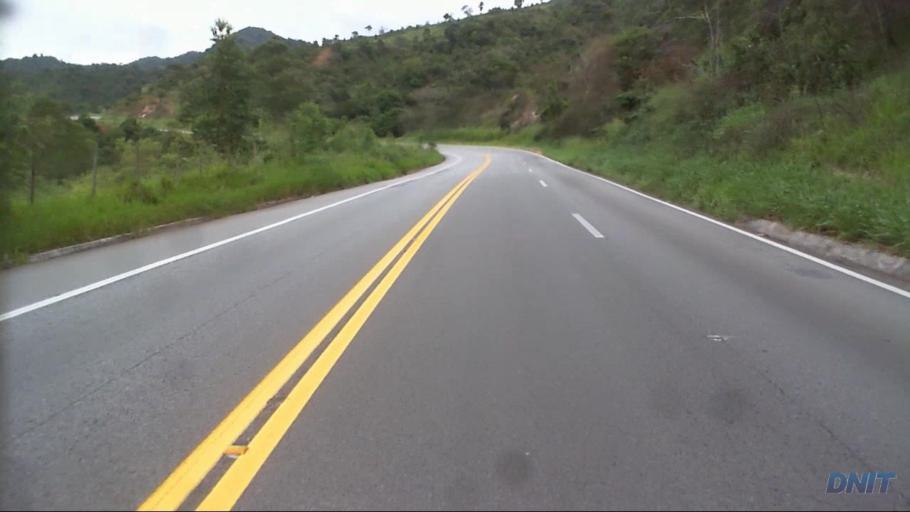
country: BR
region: Minas Gerais
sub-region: Nova Era
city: Nova Era
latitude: -19.6273
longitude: -42.8715
